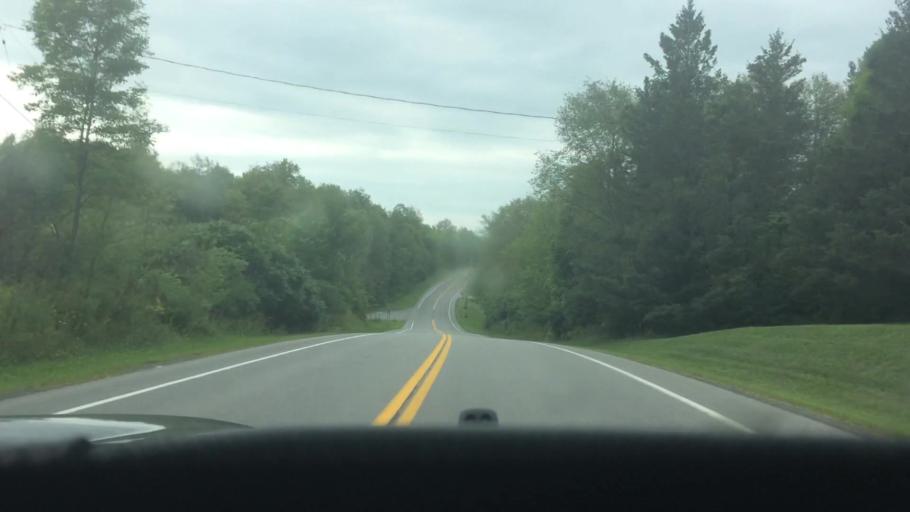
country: US
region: New York
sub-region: St. Lawrence County
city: Canton
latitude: 44.5196
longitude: -75.3379
